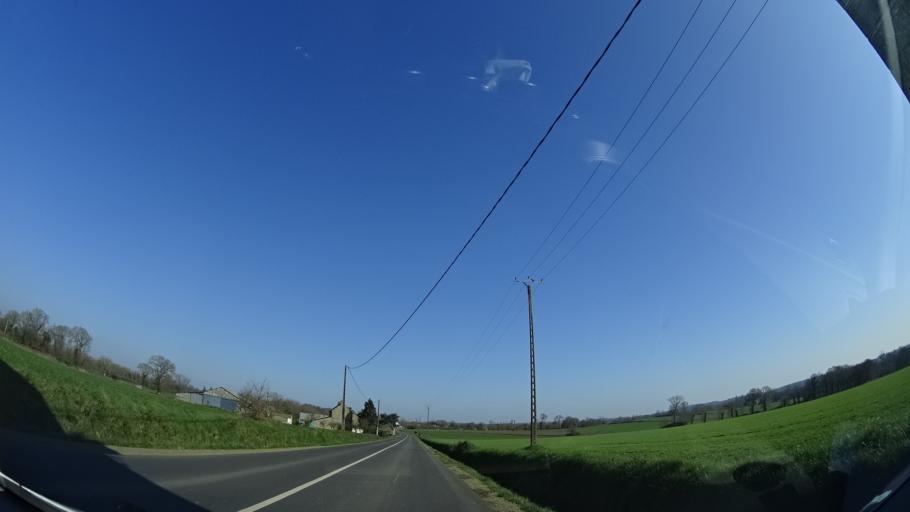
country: FR
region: Brittany
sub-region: Departement d'Ille-et-Vilaine
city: Combourg
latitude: 48.4060
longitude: -1.7716
